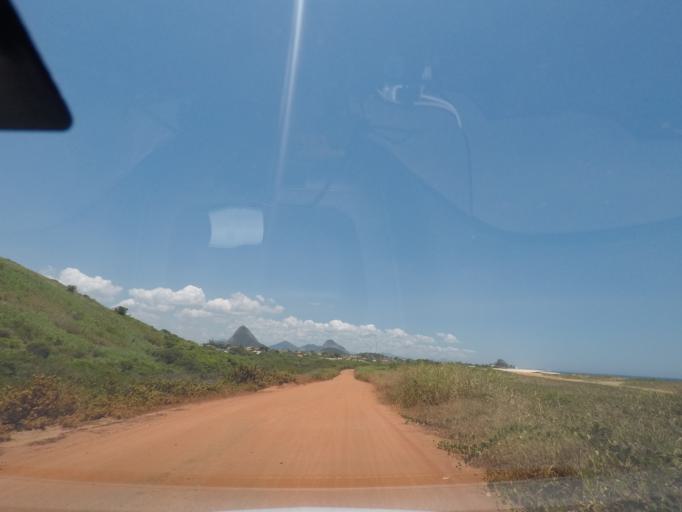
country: BR
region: Rio de Janeiro
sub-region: Niteroi
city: Niteroi
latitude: -22.9690
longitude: -43.0001
